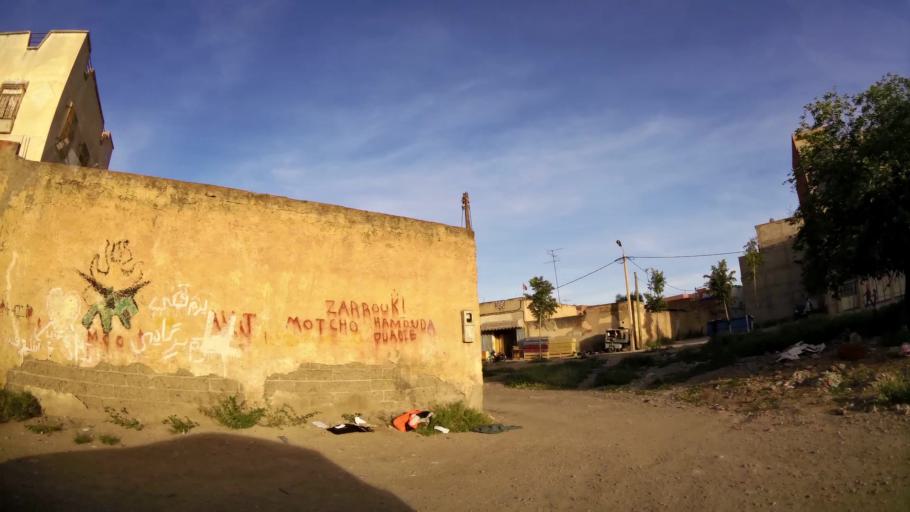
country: MA
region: Oriental
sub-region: Oujda-Angad
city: Oujda
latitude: 34.6757
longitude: -1.8998
